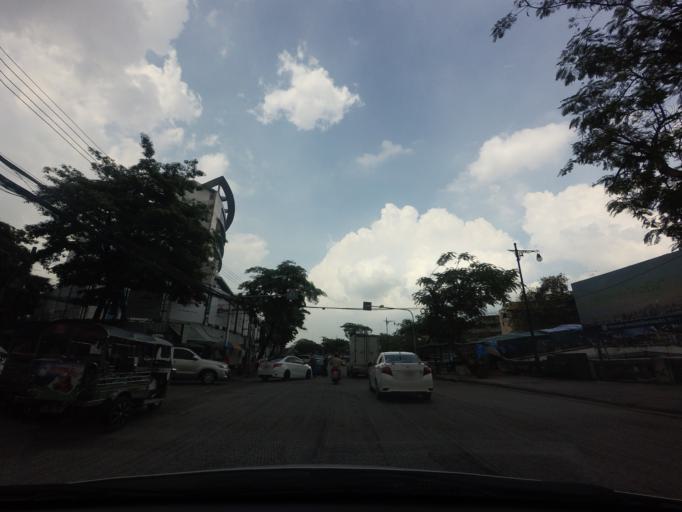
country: TH
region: Bangkok
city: Pom Prap Sattru Phai
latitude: 13.7548
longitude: 100.5170
